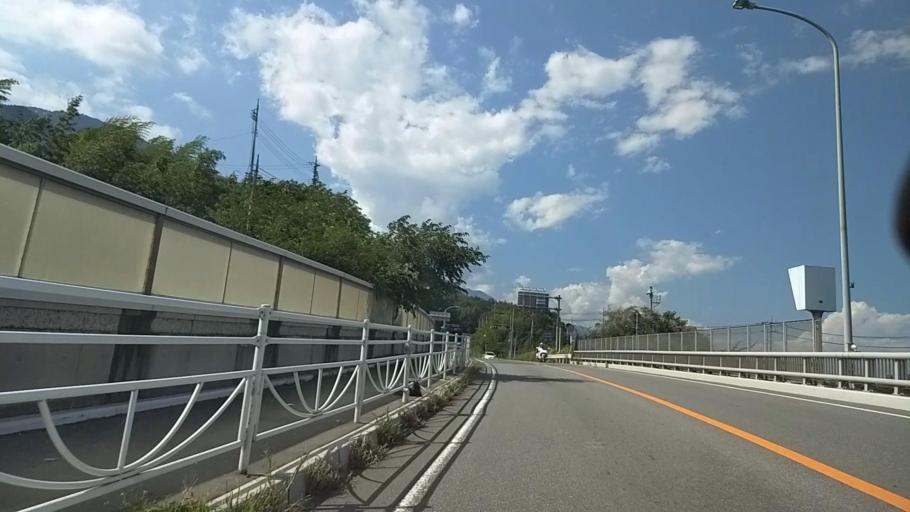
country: JP
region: Shizuoka
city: Fujinomiya
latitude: 35.3823
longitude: 138.4488
